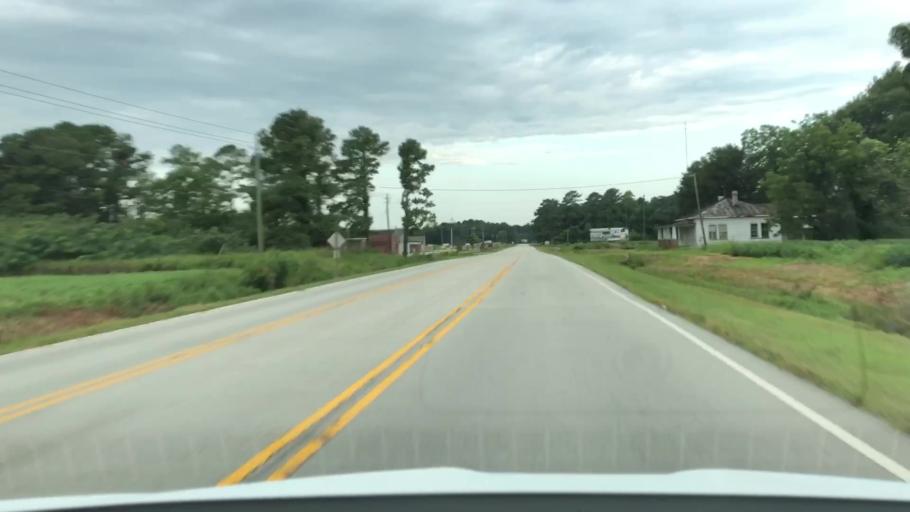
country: US
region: North Carolina
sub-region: Jones County
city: Trenton
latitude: 35.0345
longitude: -77.3303
